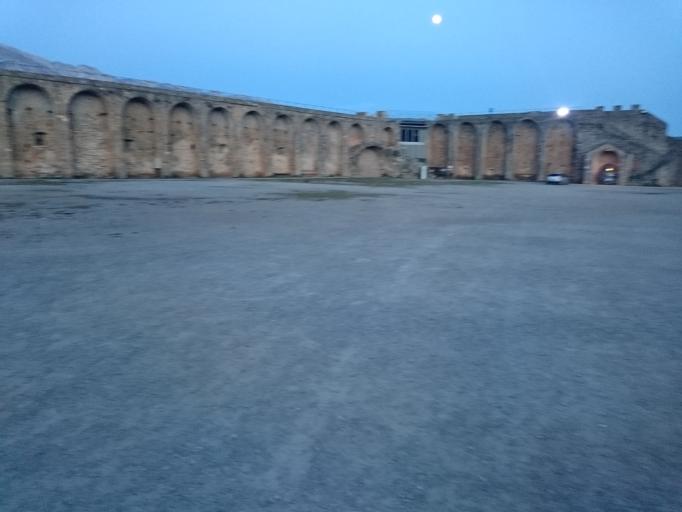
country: ES
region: Aragon
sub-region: Provincia de Huesca
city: Ainsa
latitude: 42.4182
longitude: 0.1361
